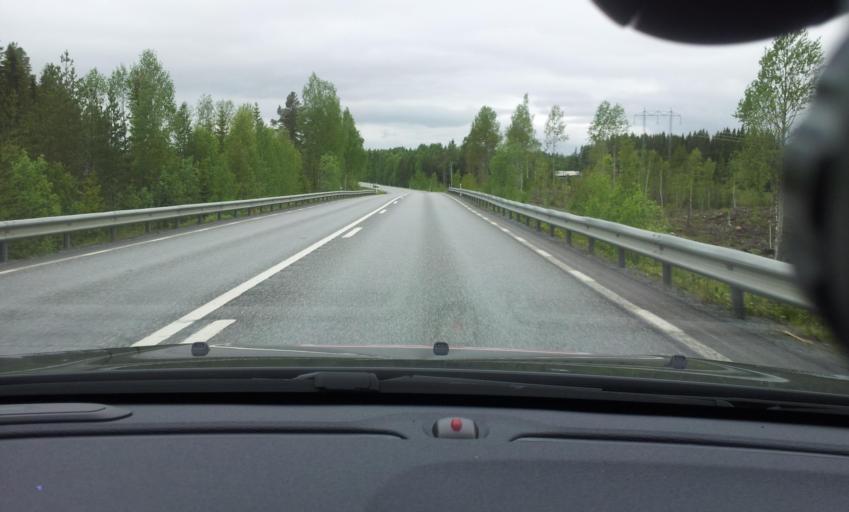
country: SE
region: Jaemtland
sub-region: Krokoms Kommun
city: Krokom
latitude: 63.3227
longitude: 14.2058
